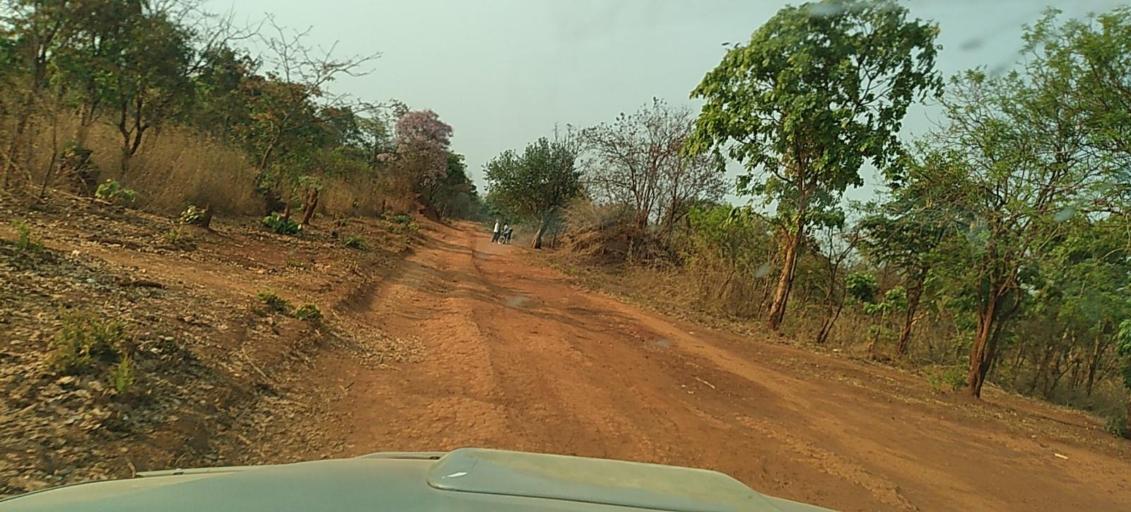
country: ZM
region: North-Western
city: Kasempa
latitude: -13.2964
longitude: 26.5544
